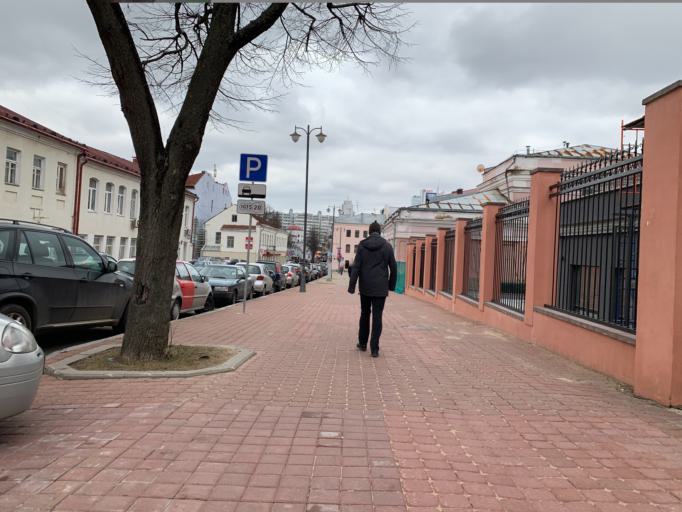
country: BY
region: Minsk
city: Minsk
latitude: 53.9005
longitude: 27.5544
